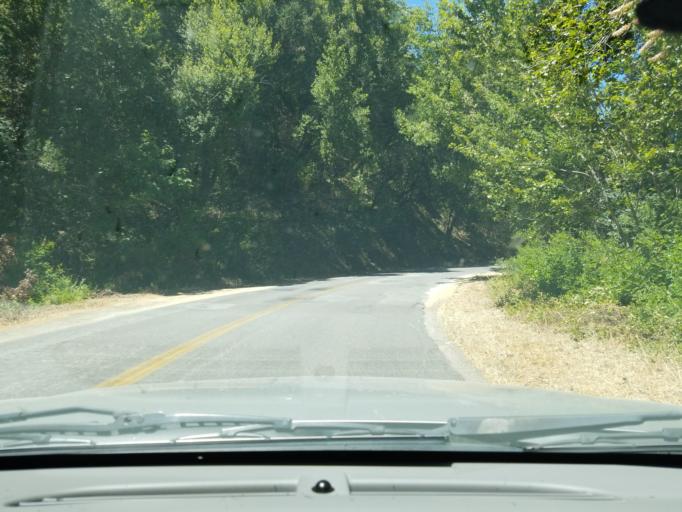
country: US
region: California
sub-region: Monterey County
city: Carmel Valley Village
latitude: 36.4446
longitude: -121.6792
